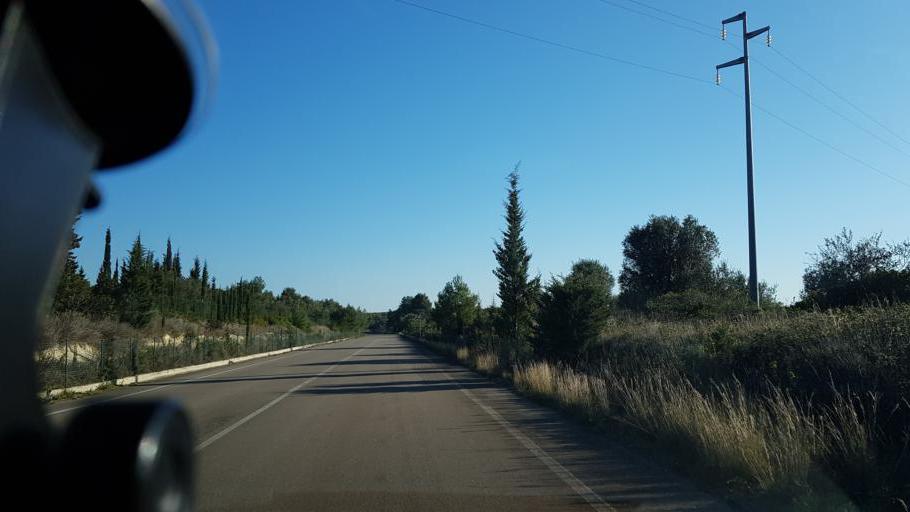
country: IT
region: Apulia
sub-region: Provincia di Lecce
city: Merine
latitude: 40.4022
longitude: 18.2496
